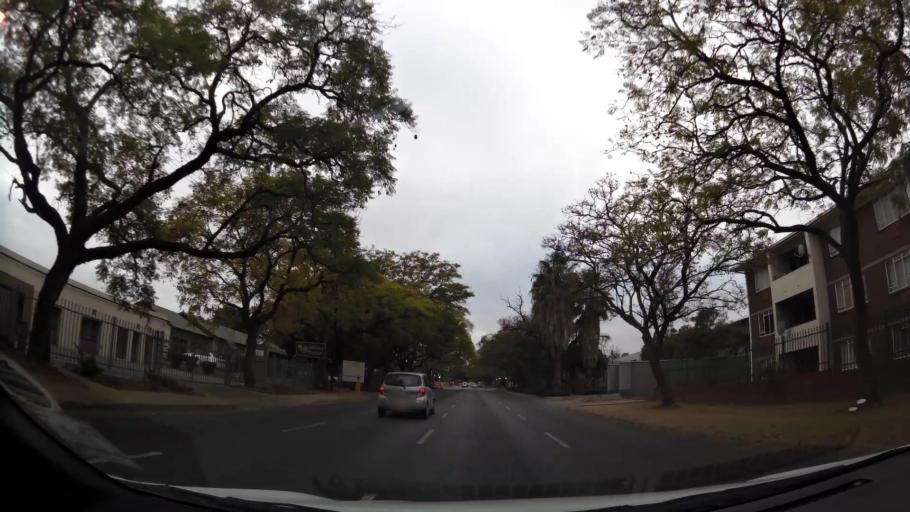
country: ZA
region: Limpopo
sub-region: Capricorn District Municipality
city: Polokwane
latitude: -23.9020
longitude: 29.4536
